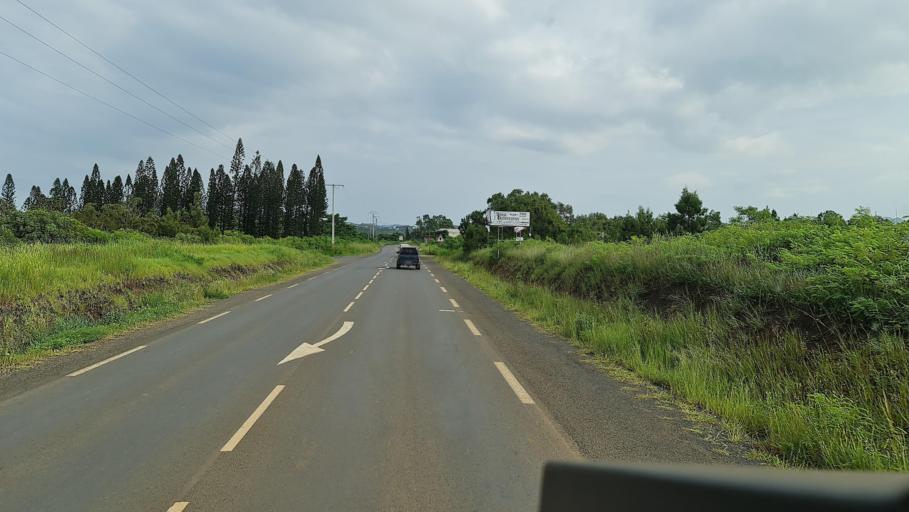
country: NC
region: North Province
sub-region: Koumac
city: Koumac
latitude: -20.5768
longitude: 164.3017
